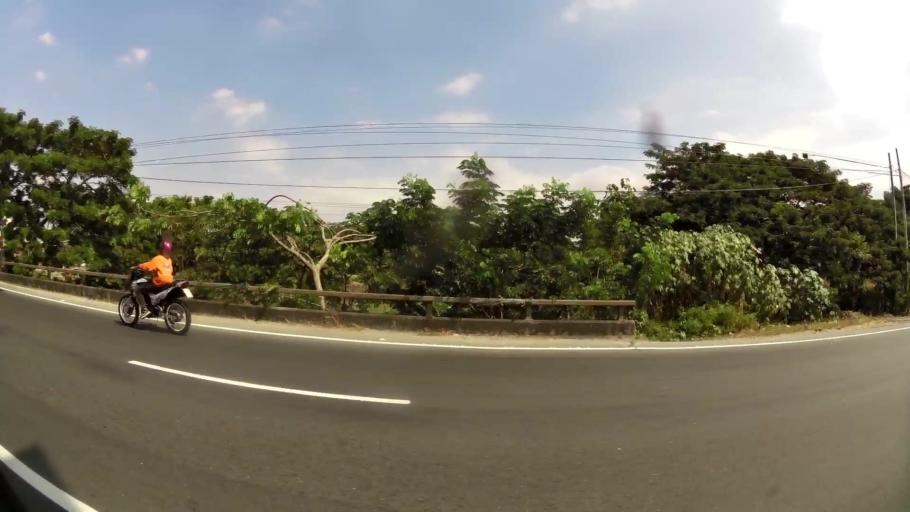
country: EC
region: Guayas
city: Eloy Alfaro
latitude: -2.0519
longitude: -79.8832
